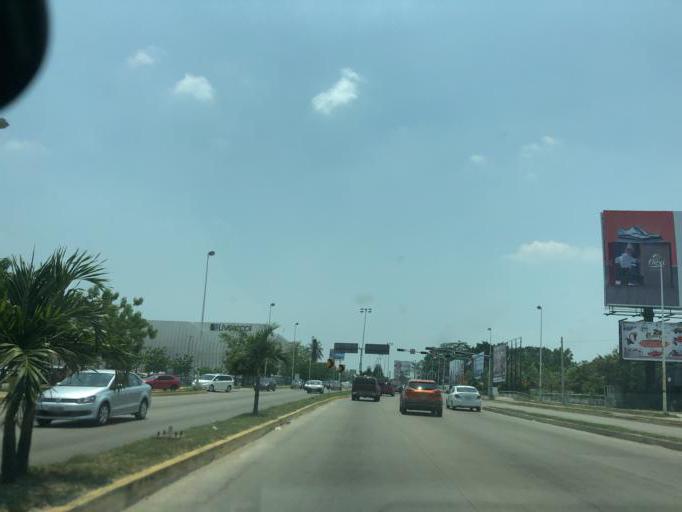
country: MX
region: Tabasco
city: Villahermosa
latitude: 17.9676
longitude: -92.9384
